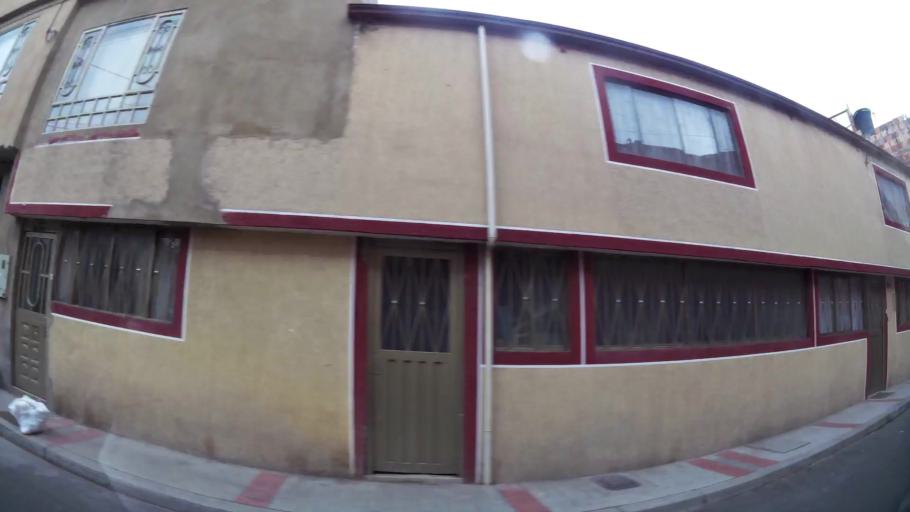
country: CO
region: Bogota D.C.
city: Barrio San Luis
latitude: 4.7039
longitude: -74.0889
